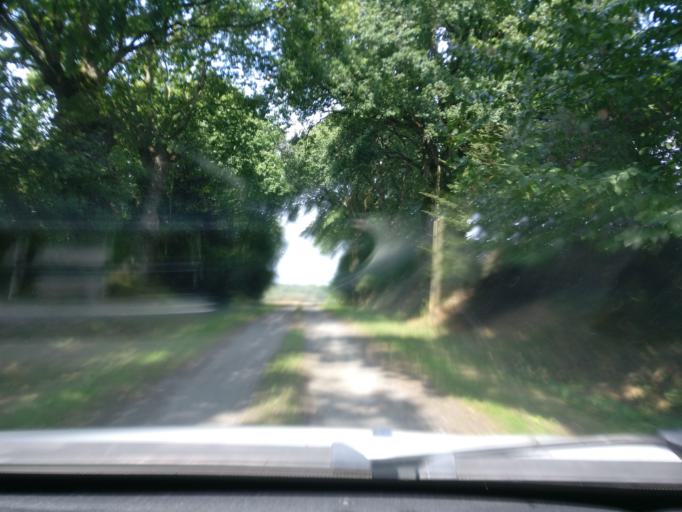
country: FR
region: Brittany
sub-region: Departement d'Ille-et-Vilaine
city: Gosne
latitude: 48.2626
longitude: -1.4844
